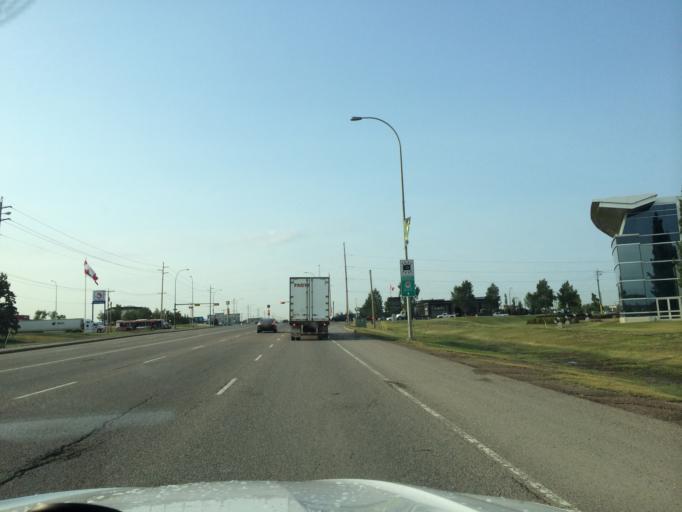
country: CA
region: Alberta
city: Calgary
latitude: 51.0830
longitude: -114.0020
